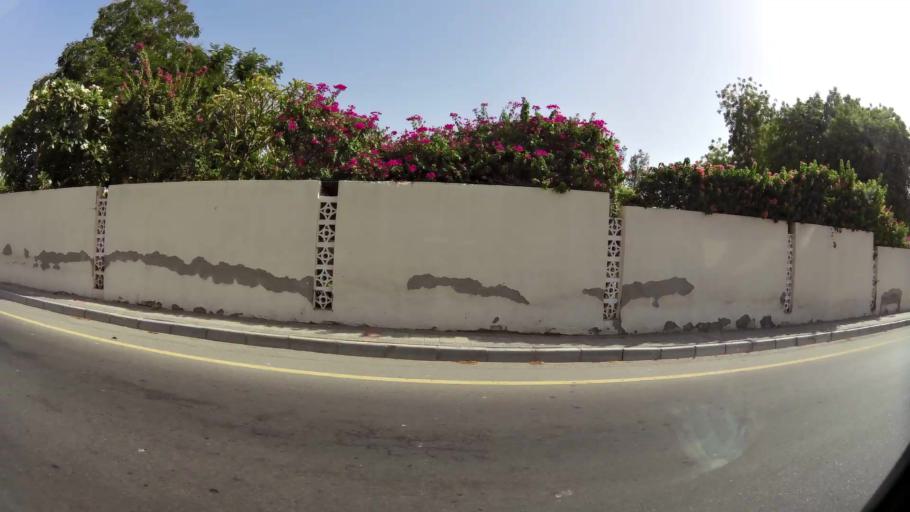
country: OM
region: Muhafazat Masqat
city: Muscat
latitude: 23.6158
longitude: 58.5135
